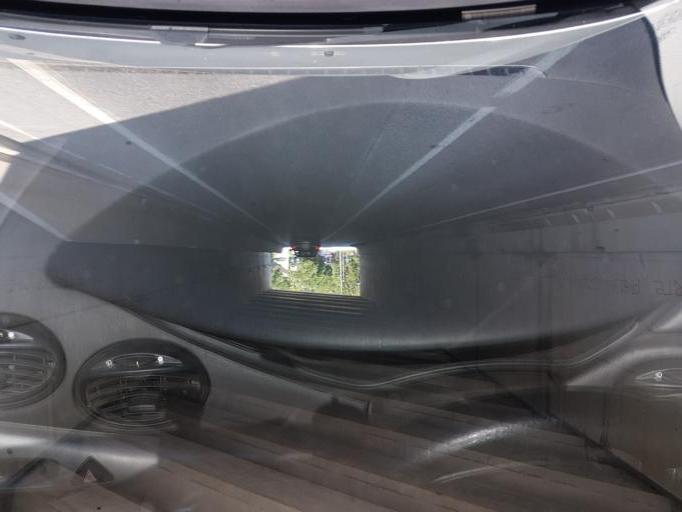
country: SI
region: Koper-Capodistria
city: Spodnje Skofije
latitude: 45.5959
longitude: 13.8055
